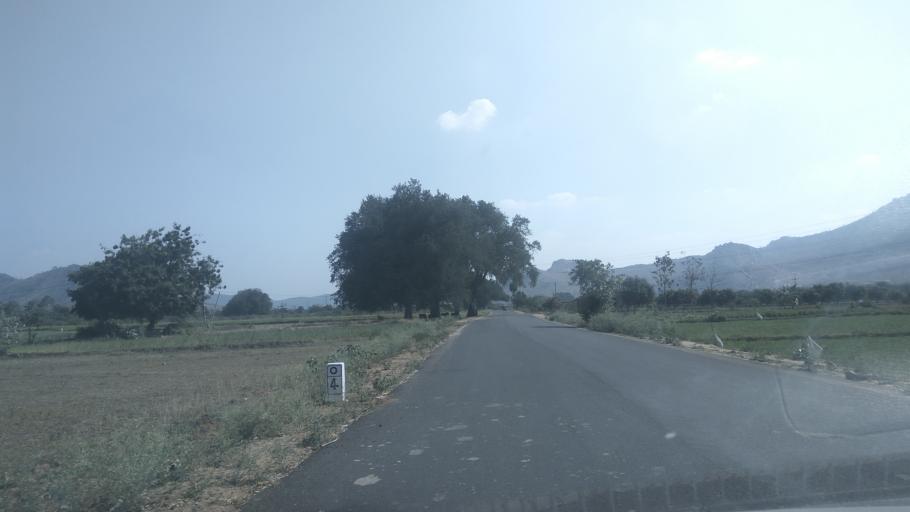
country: IN
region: Andhra Pradesh
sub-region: Chittoor
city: Renigunta
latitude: 13.5512
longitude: 79.4823
